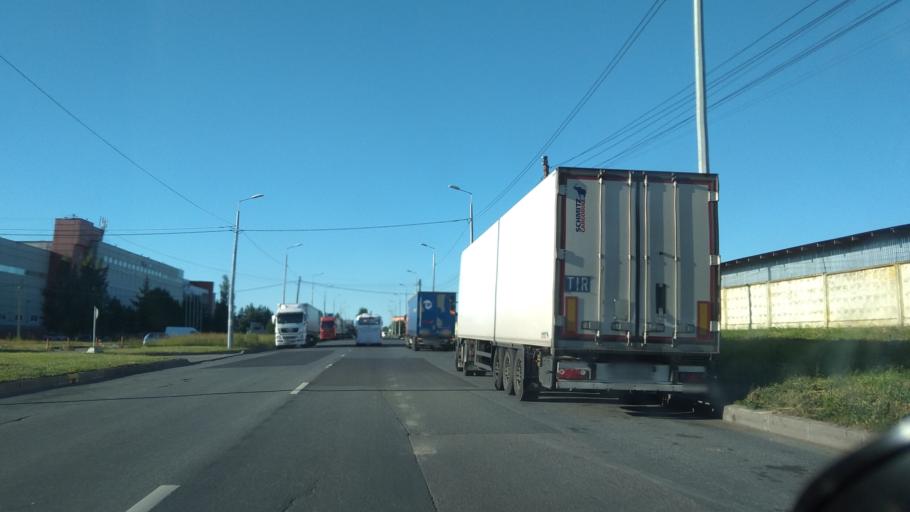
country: RU
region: Leningrad
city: Bugry
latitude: 60.0709
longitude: 30.3729
